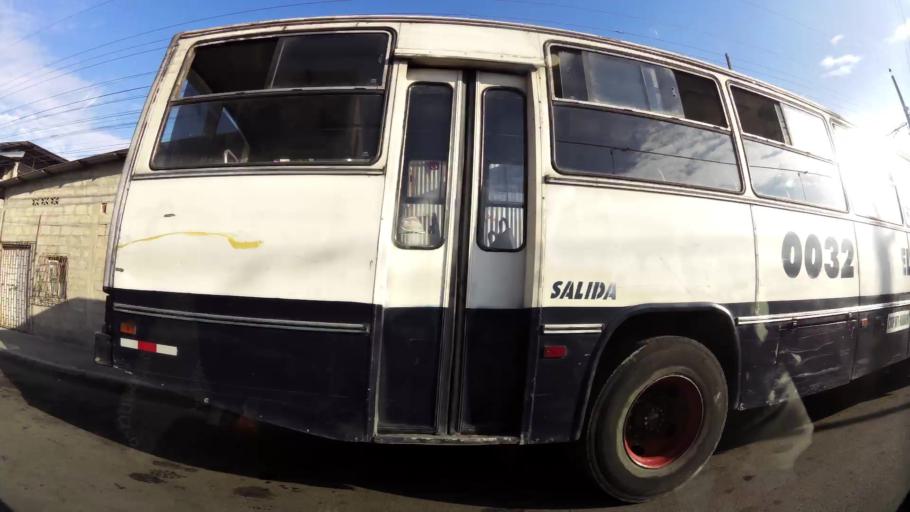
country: EC
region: Guayas
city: Guayaquil
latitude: -2.2277
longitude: -79.9131
